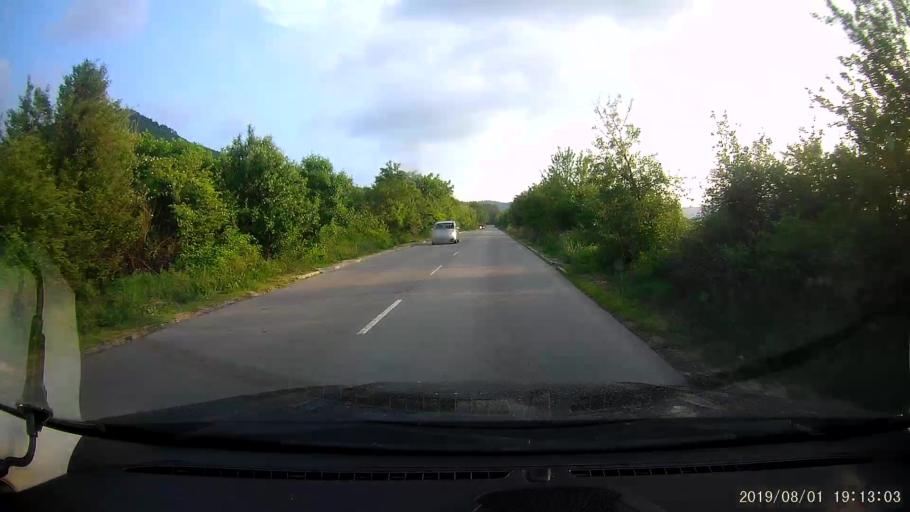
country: BG
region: Shumen
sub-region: Obshtina Smyadovo
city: Smyadovo
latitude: 42.9562
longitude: 26.9446
